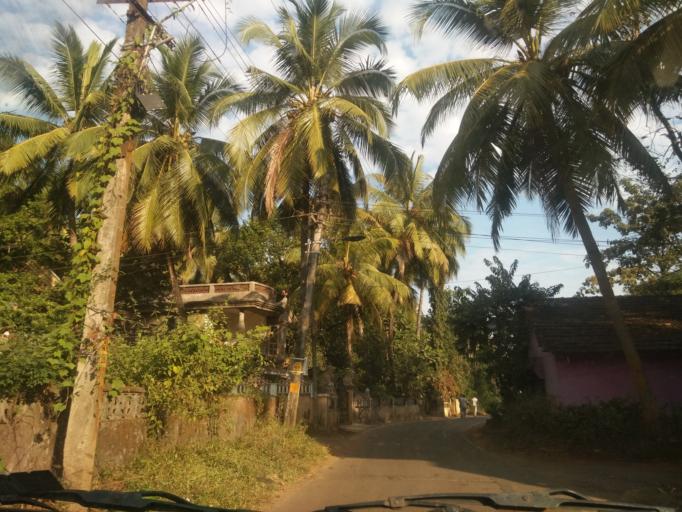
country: IN
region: Goa
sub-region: South Goa
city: Madgaon
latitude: 15.2562
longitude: 73.9555
